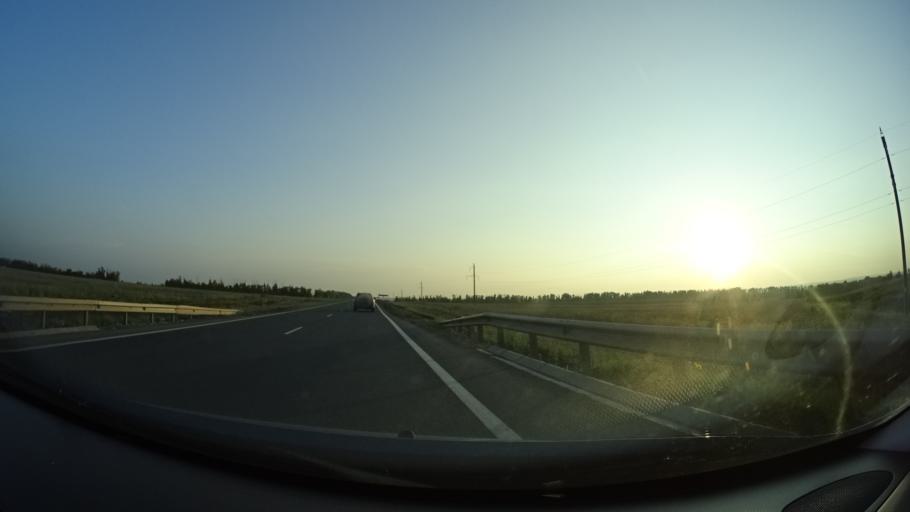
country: RU
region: Samara
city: Sernovodsk
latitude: 53.9591
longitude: 51.4062
